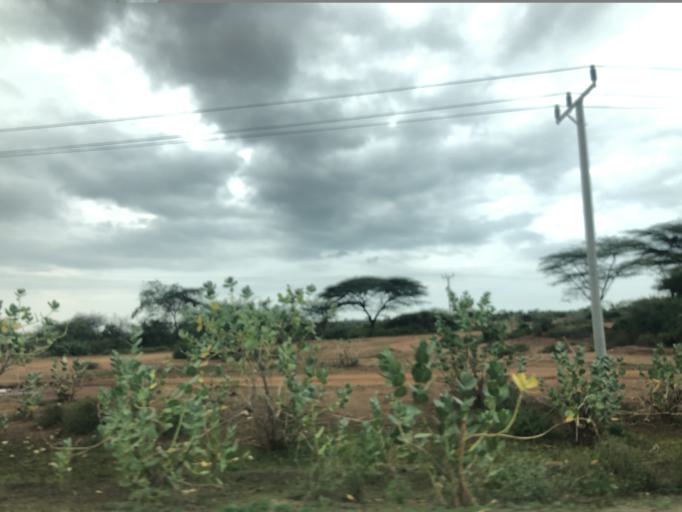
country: ET
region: Southern Nations, Nationalities, and People's Region
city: Turmi
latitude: 5.0178
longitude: 36.4852
